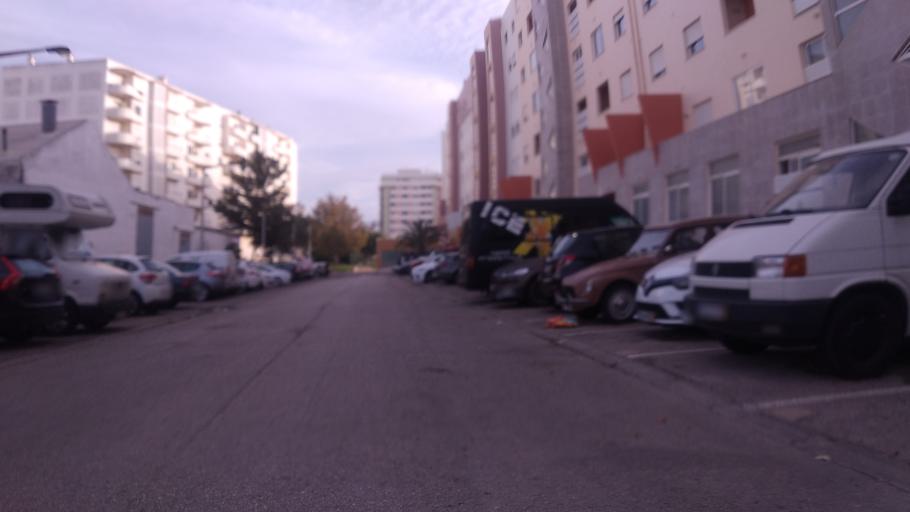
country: PT
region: Faro
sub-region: Faro
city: Faro
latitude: 37.0268
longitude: -7.9408
